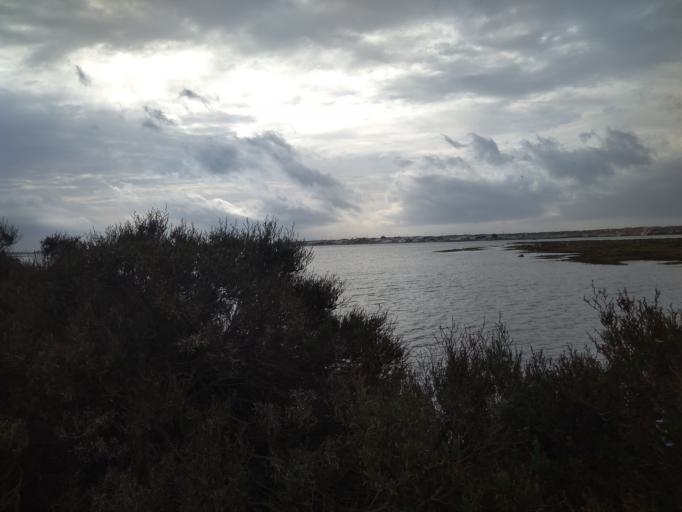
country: PT
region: Faro
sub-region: Loule
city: Almancil
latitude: 37.0202
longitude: -8.0041
